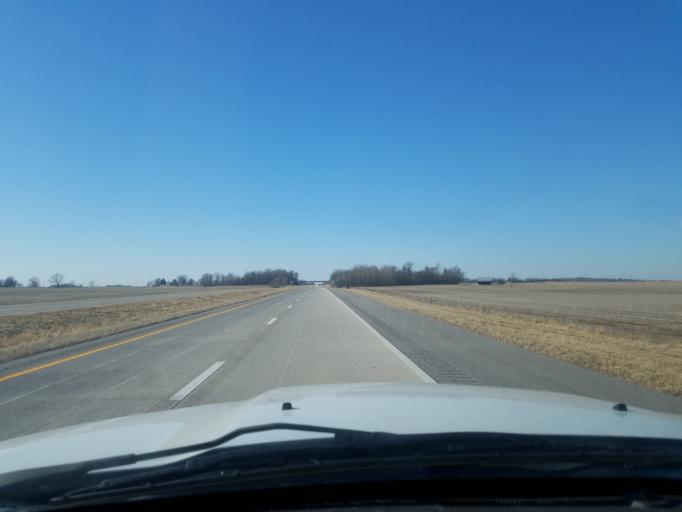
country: US
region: Kentucky
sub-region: Henderson County
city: Henderson
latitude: 37.7910
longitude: -87.4860
